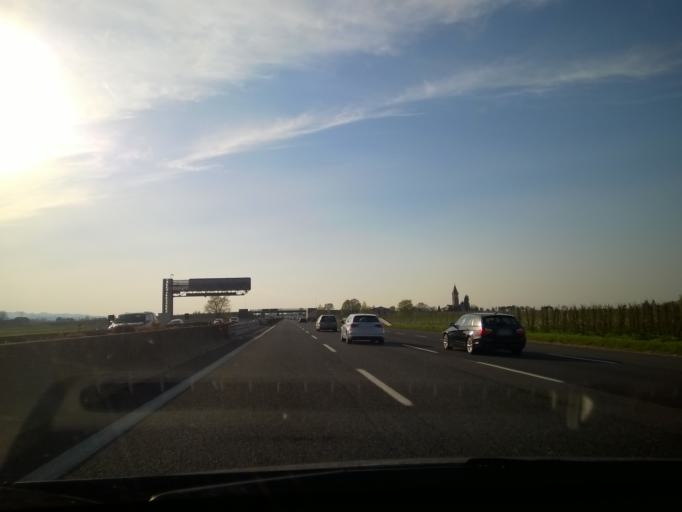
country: IT
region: Emilia-Romagna
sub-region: Provincia di Ravenna
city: Castel Bolognese
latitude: 44.3573
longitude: 11.8047
